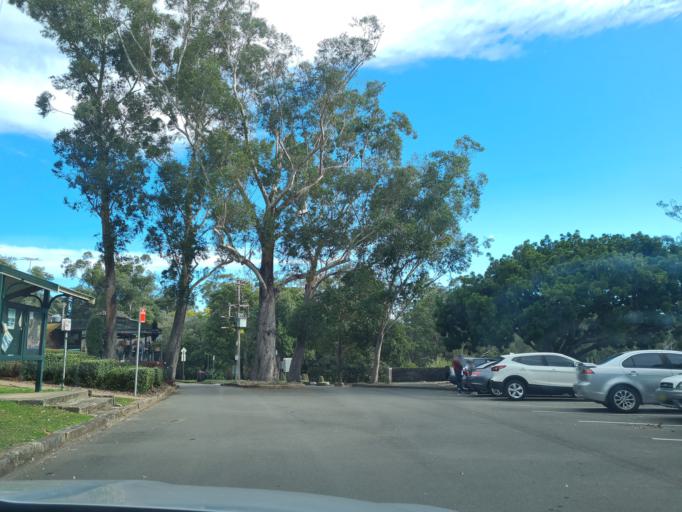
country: AU
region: New South Wales
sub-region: Parramatta
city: Northmead
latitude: -33.7911
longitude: 151.0076
